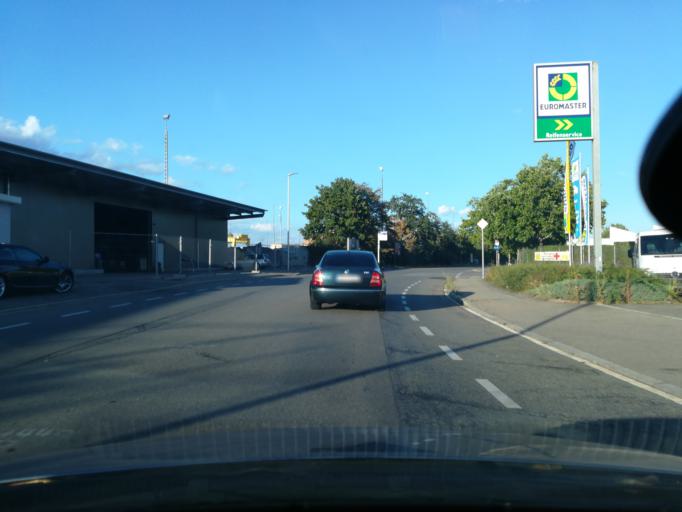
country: DE
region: Baden-Wuerttemberg
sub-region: Freiburg Region
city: Singen
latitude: 47.7574
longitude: 8.8594
